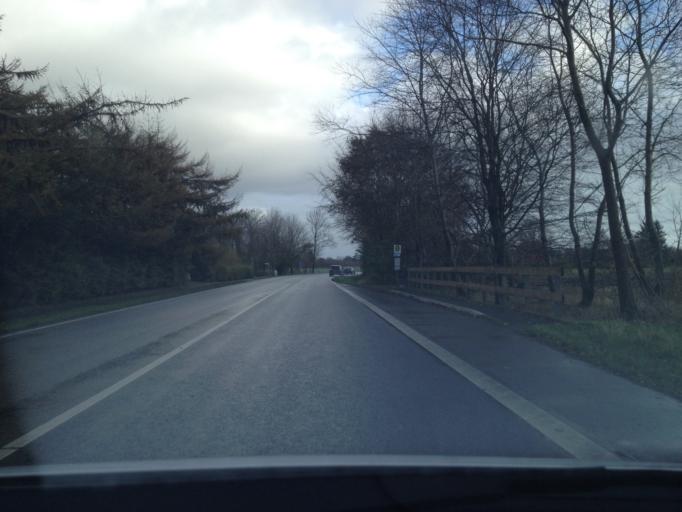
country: DE
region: Schleswig-Holstein
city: Klixbull
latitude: 54.7933
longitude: 8.9147
